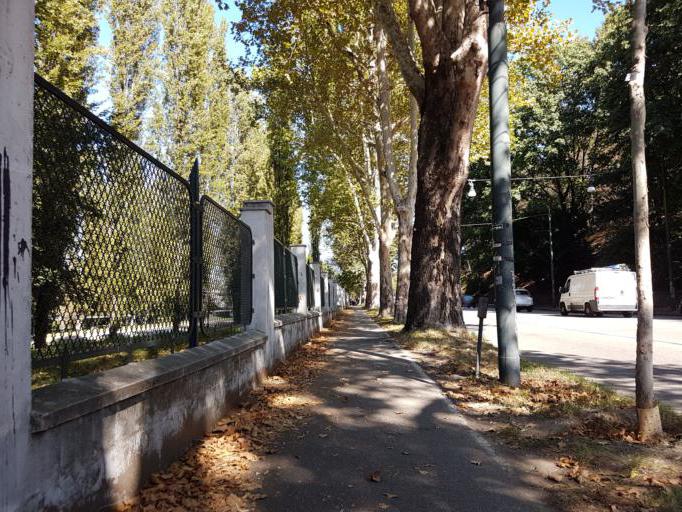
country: IT
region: Piedmont
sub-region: Provincia di Torino
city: Turin
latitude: 45.0600
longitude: 7.6954
